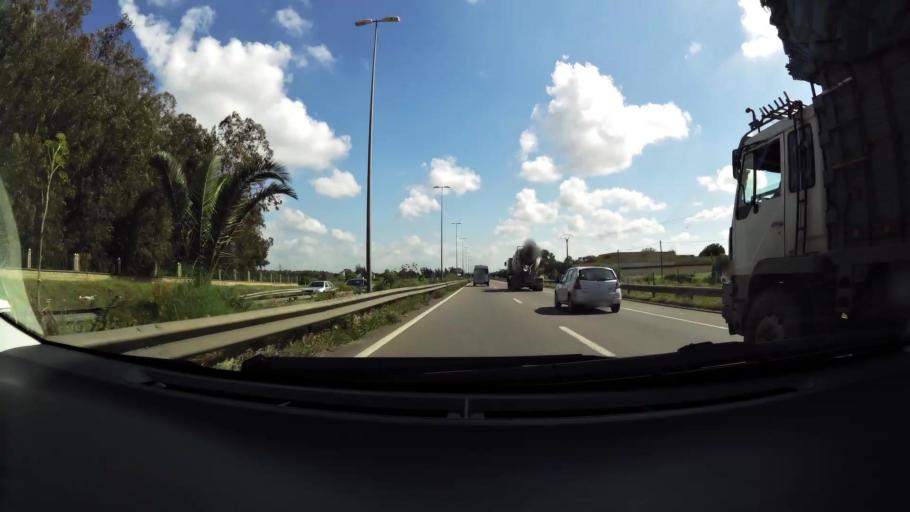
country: MA
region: Grand Casablanca
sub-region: Nouaceur
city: Bouskoura
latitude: 33.4685
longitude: -7.6334
